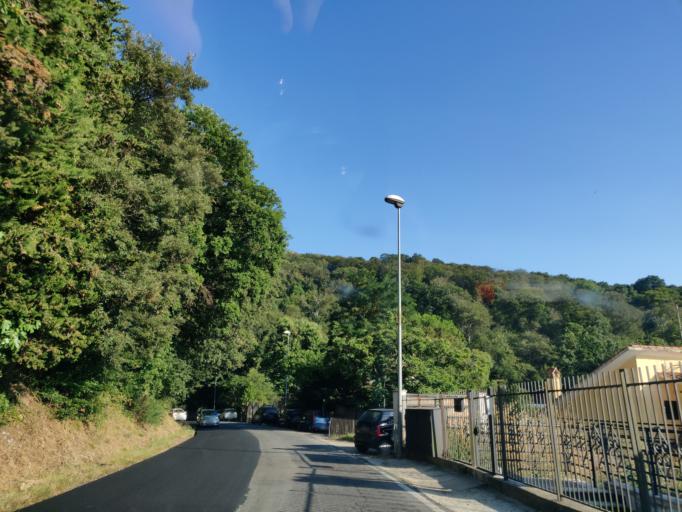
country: IT
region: Latium
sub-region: Citta metropolitana di Roma Capitale
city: Allumiere
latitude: 42.1543
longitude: 11.9066
